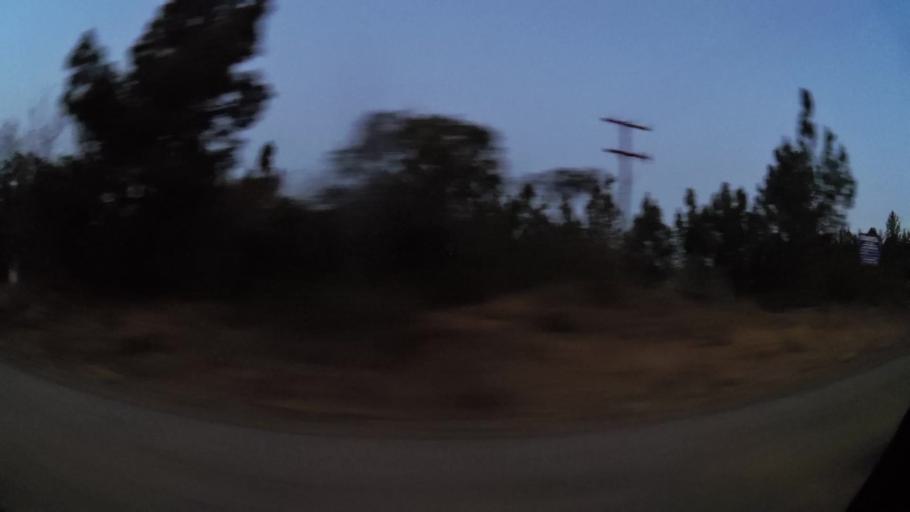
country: ZA
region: Gauteng
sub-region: City of Johannesburg Metropolitan Municipality
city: Midrand
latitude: -25.9632
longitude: 28.0812
